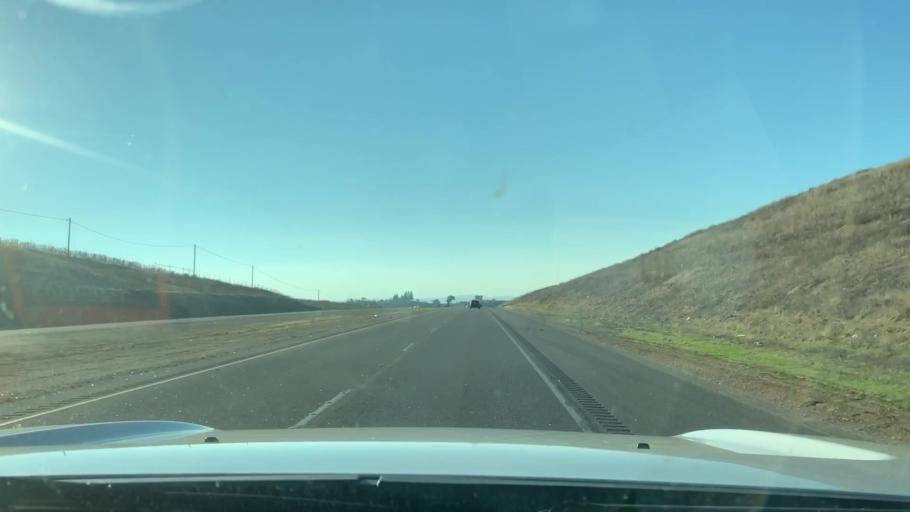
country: US
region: California
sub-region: San Luis Obispo County
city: Shandon
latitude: 35.6553
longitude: -120.5234
